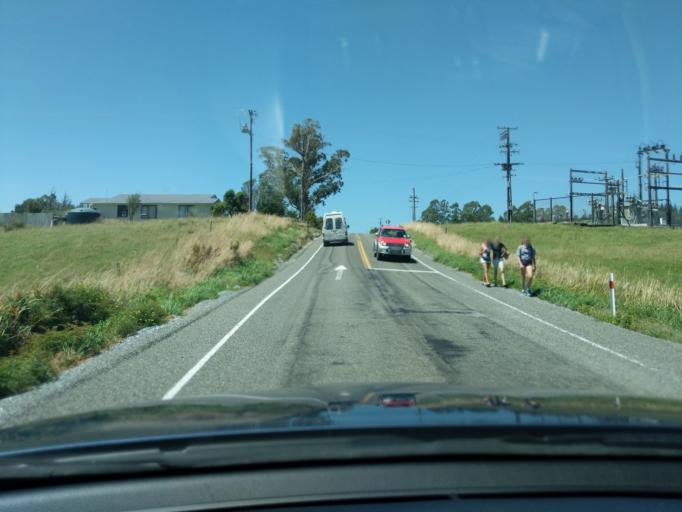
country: NZ
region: Tasman
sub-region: Tasman District
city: Takaka
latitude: -40.6867
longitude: 172.6512
